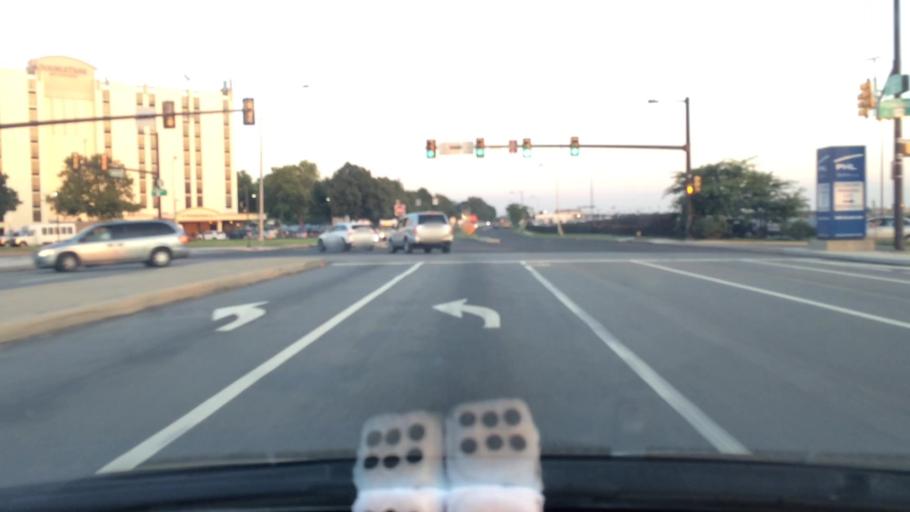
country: US
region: Pennsylvania
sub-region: Delaware County
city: Colwyn
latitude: 39.8901
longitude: -75.2340
